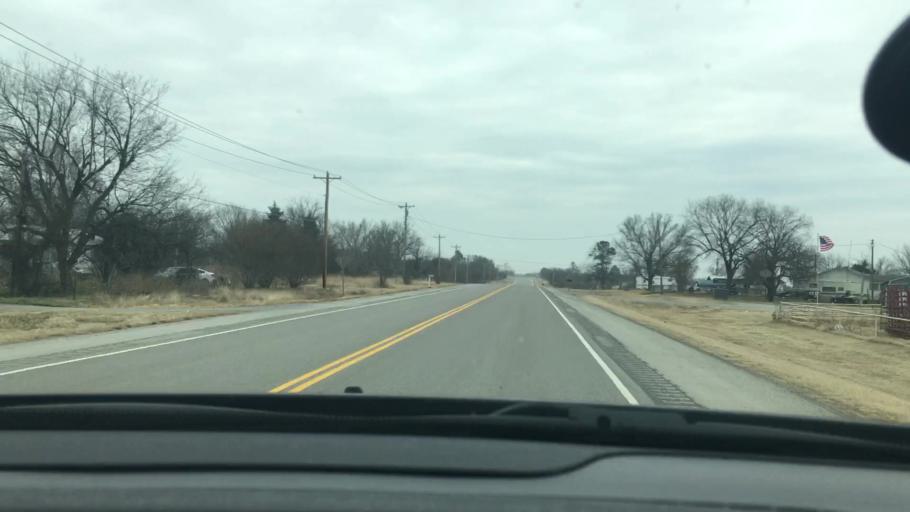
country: US
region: Oklahoma
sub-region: Carter County
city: Healdton
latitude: 34.4043
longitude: -97.5084
